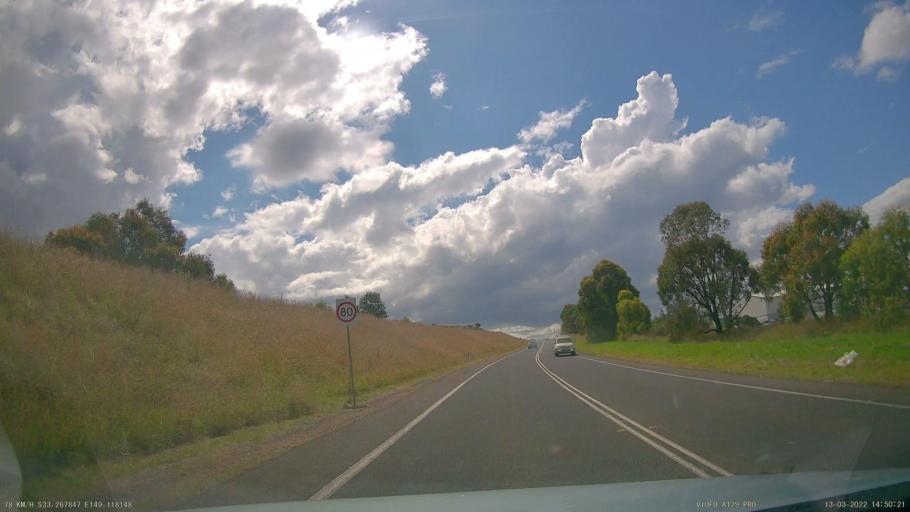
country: AU
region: New South Wales
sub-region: Orange Municipality
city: Orange
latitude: -33.2677
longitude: 149.1181
